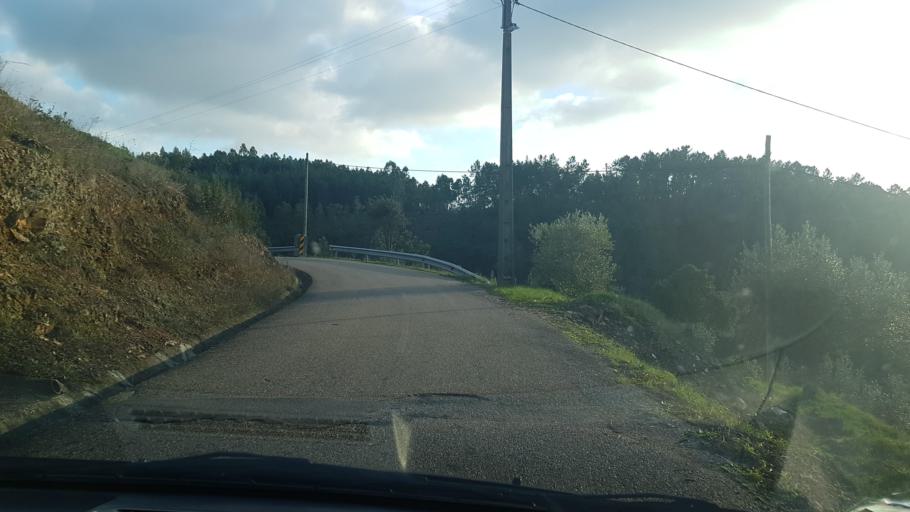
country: PT
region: Castelo Branco
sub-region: Vila de Rei
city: Vila de Rei
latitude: 39.5996
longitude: -8.1207
